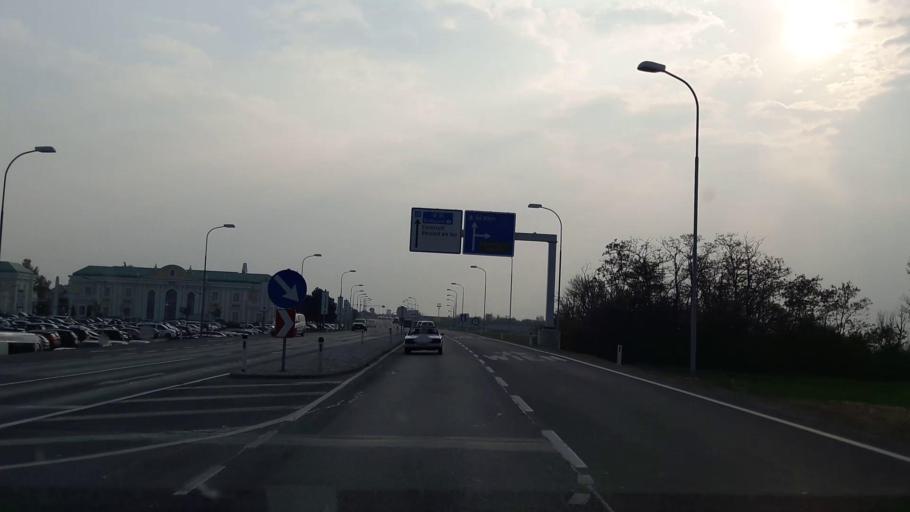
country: AT
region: Burgenland
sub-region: Politischer Bezirk Neusiedl am See
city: Parndorf
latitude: 47.9817
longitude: 16.8476
